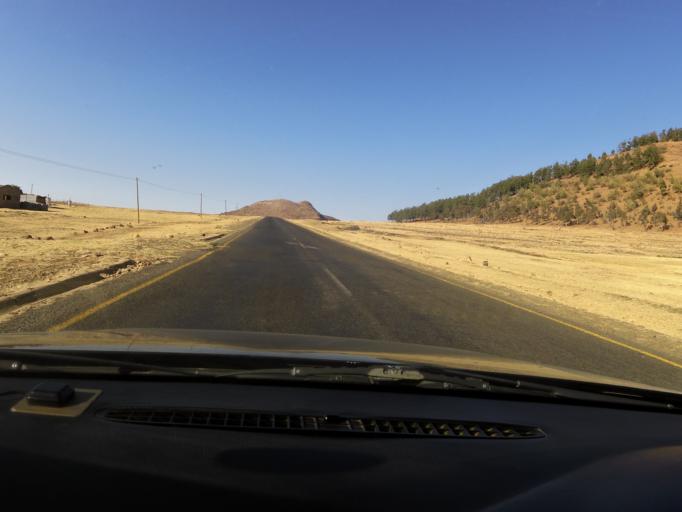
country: LS
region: Mafeteng
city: Mafeteng
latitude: -29.9090
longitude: 27.2497
